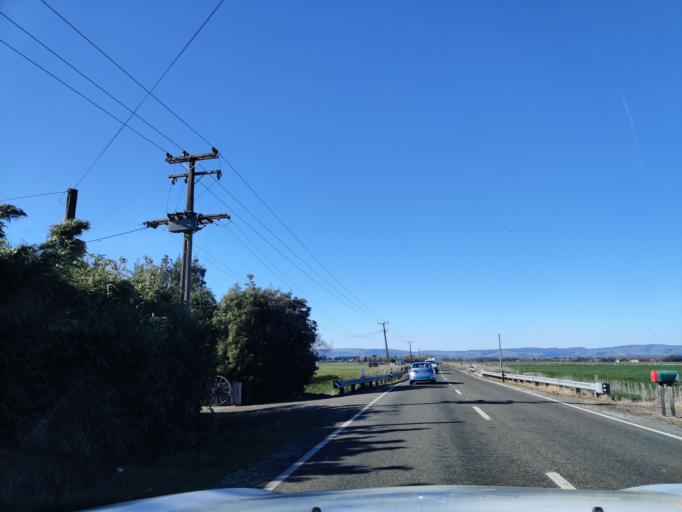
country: NZ
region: Manawatu-Wanganui
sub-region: Palmerston North City
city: Palmerston North
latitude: -40.2855
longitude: 175.5610
